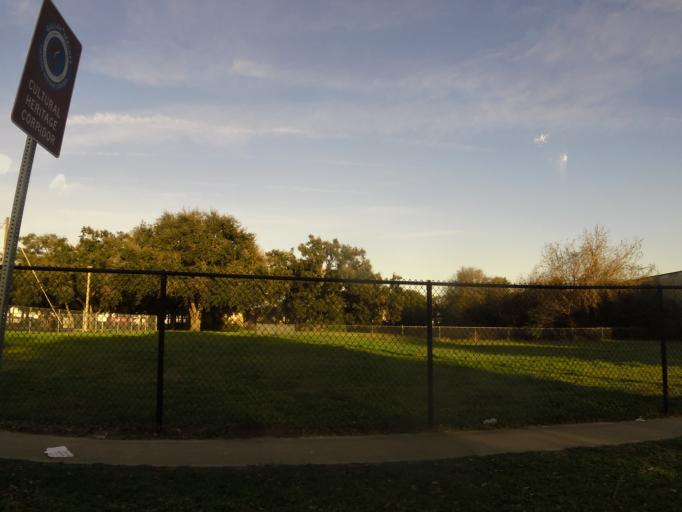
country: US
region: Florida
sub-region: Duval County
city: Jacksonville
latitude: 30.3410
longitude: -81.6388
